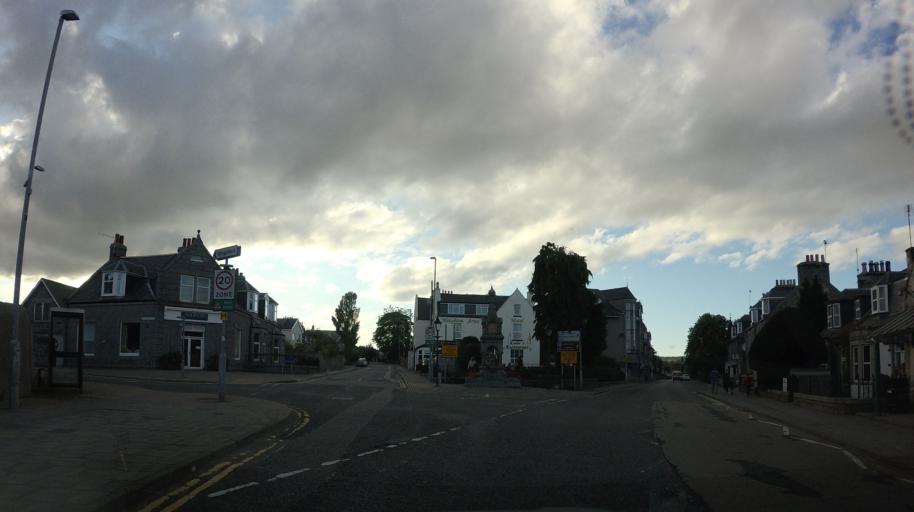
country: GB
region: Scotland
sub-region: Aberdeenshire
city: Alford
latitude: 57.2319
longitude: -2.7019
